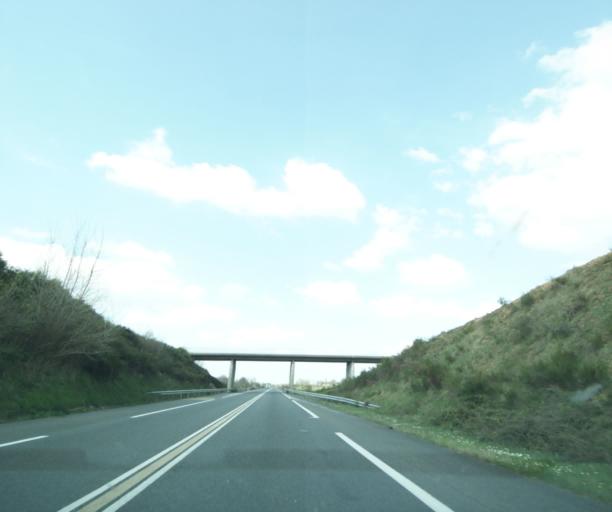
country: FR
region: Auvergne
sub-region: Departement de l'Allier
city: Montmarault
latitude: 46.3826
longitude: 3.0312
